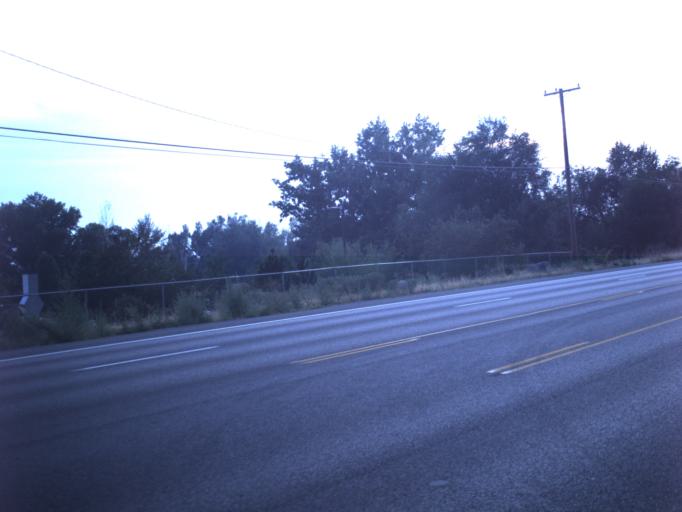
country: US
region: Utah
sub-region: Utah County
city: Springville
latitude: 40.2039
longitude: -111.6247
